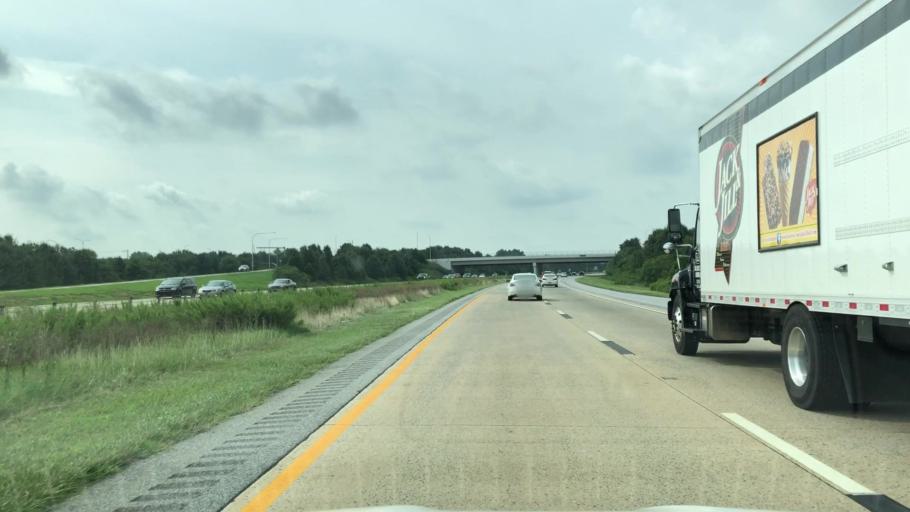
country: US
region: Delaware
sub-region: New Castle County
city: Middletown
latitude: 39.5037
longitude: -75.6461
